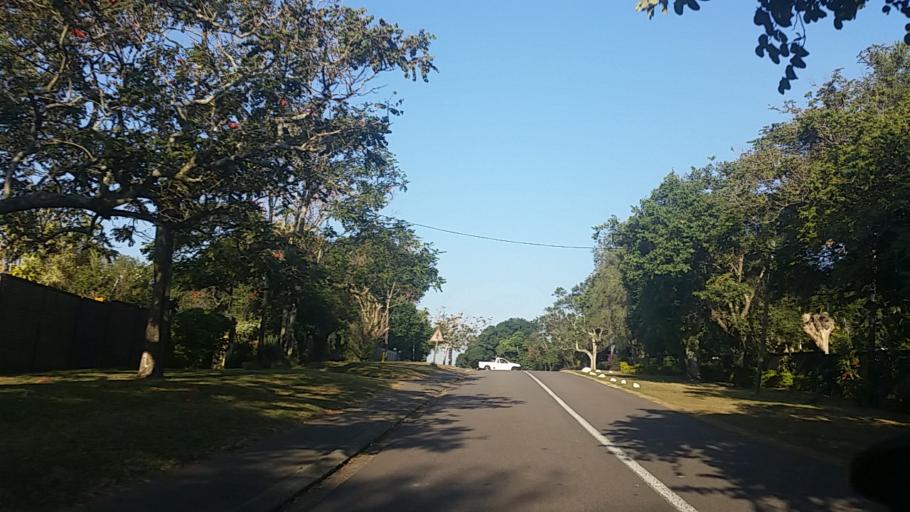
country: ZA
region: KwaZulu-Natal
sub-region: eThekwini Metropolitan Municipality
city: Berea
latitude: -29.8412
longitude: 30.9214
